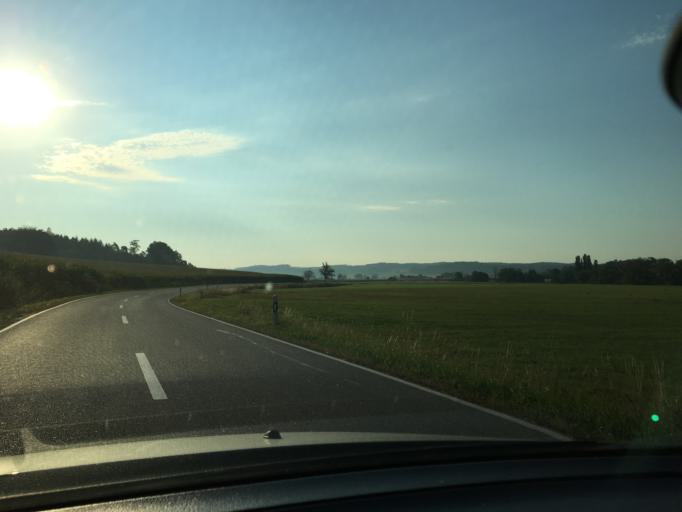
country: DE
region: Bavaria
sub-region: Lower Bavaria
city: Schalkham
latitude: 48.4990
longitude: 12.3942
